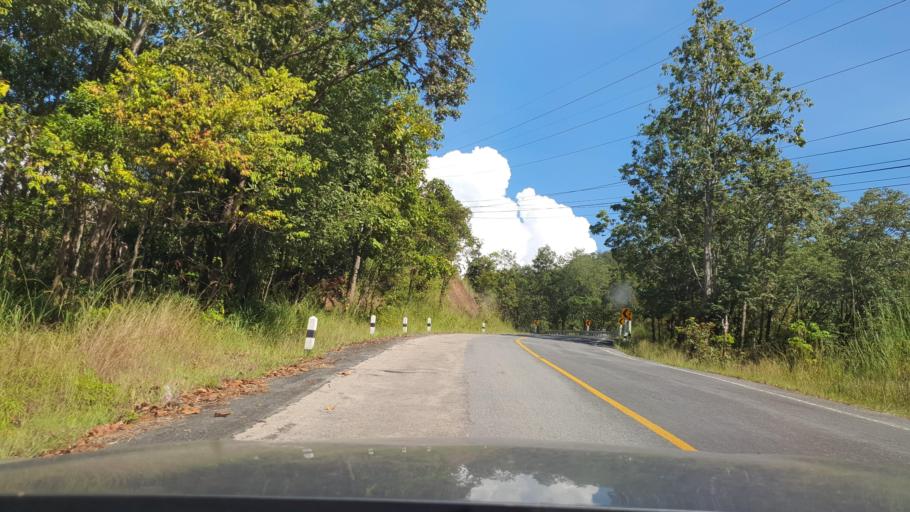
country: TH
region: Chiang Mai
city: Phrao
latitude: 19.3590
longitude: 99.2650
